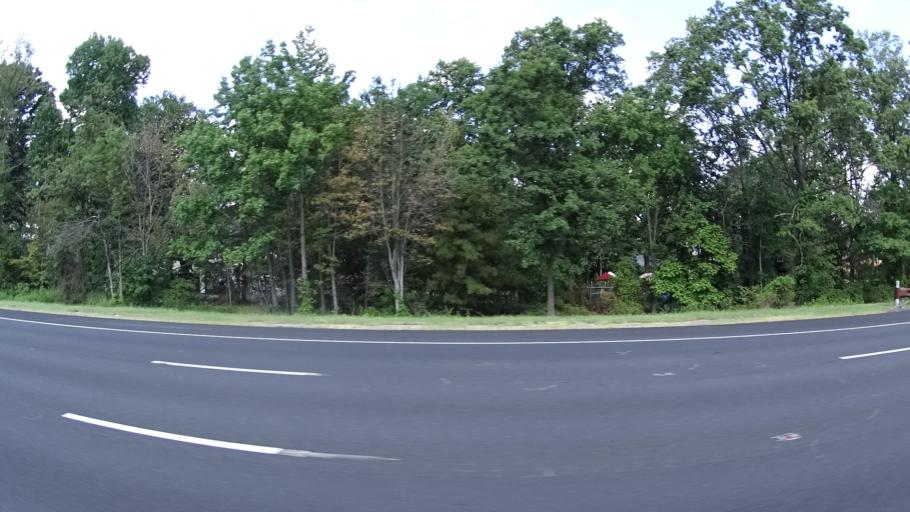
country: US
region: New Jersey
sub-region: Middlesex County
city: Iselin
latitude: 40.5932
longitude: -74.3231
